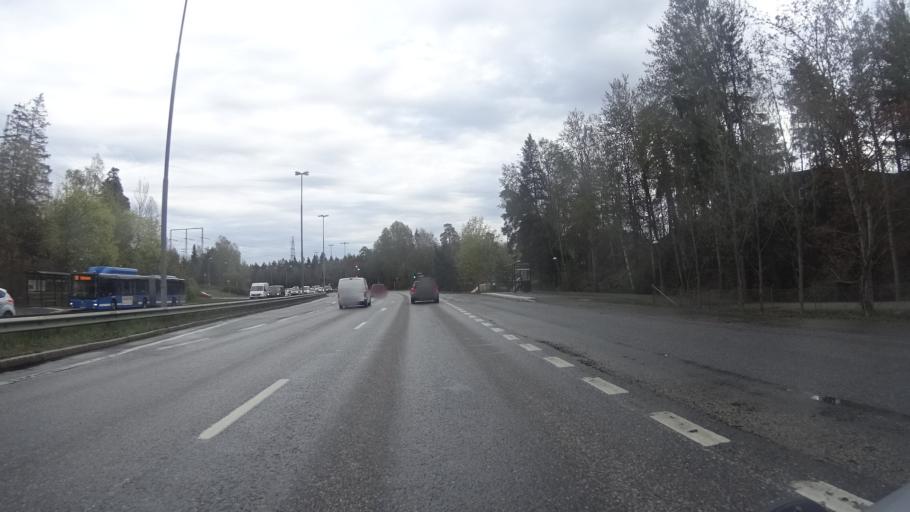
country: SE
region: Stockholm
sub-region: Stockholms Kommun
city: Arsta
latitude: 59.2639
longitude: 18.0633
